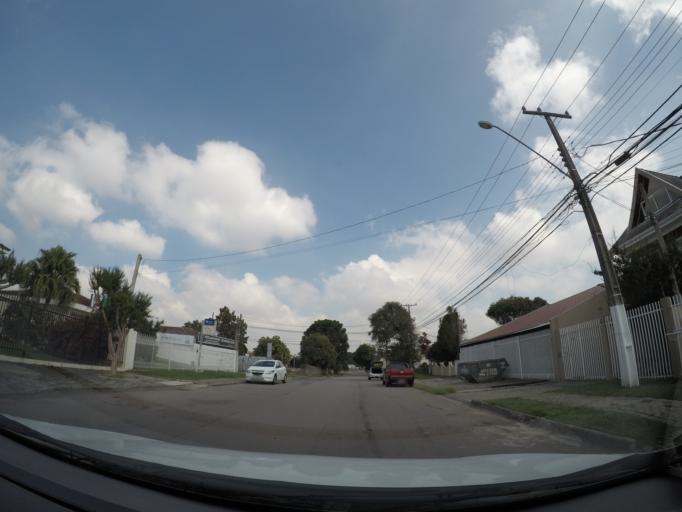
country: BR
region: Parana
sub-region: Sao Jose Dos Pinhais
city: Sao Jose dos Pinhais
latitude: -25.5024
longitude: -49.2462
